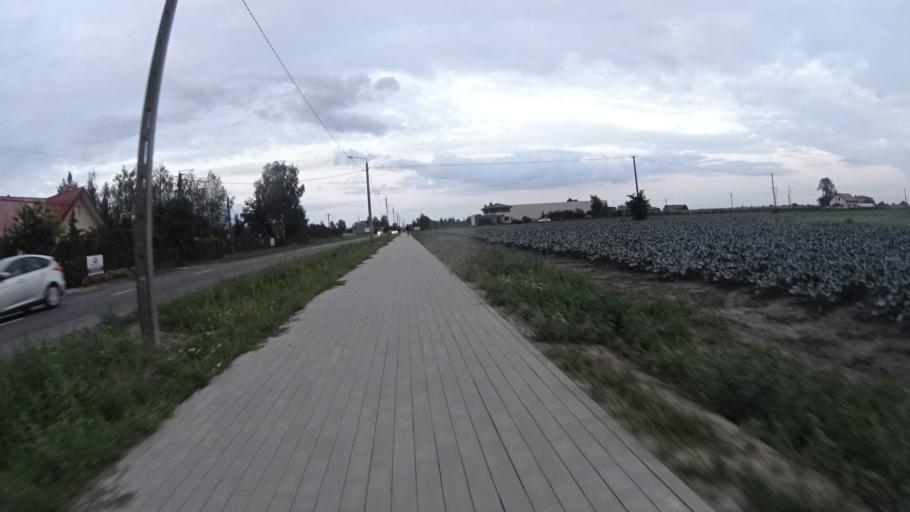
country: PL
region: Masovian Voivodeship
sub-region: Powiat warszawski zachodni
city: Ozarow Mazowiecki
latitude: 52.2308
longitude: 20.7760
